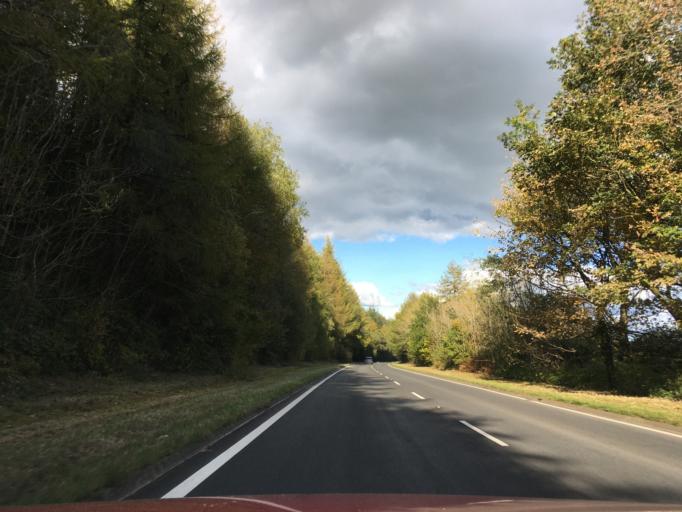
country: GB
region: Wales
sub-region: Sir Powys
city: Brecon
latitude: 51.9011
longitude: -3.4897
